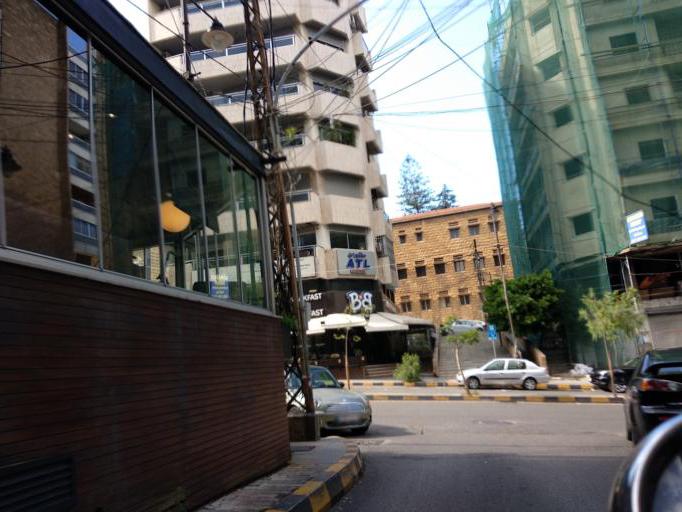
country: LB
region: Beyrouth
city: Beirut
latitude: 33.8877
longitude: 35.5234
